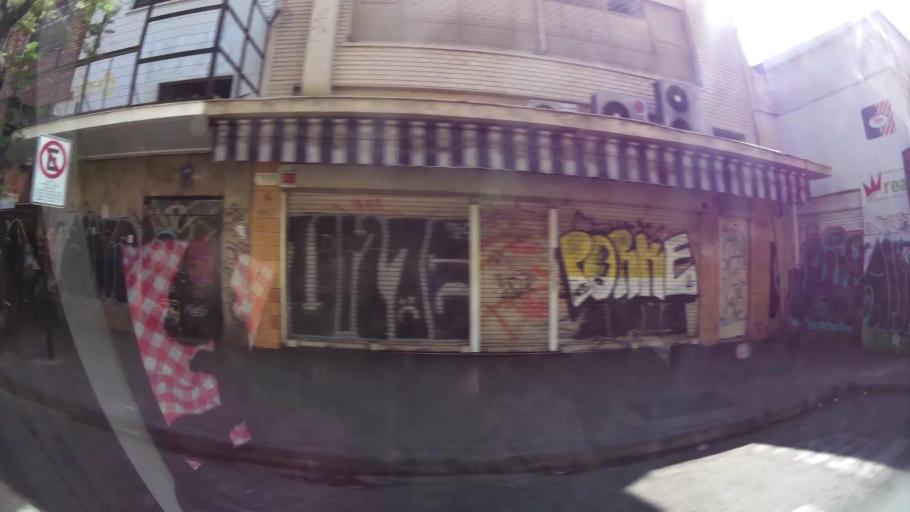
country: CL
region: Santiago Metropolitan
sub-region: Provincia de Santiago
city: Santiago
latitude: -33.4501
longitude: -70.6780
